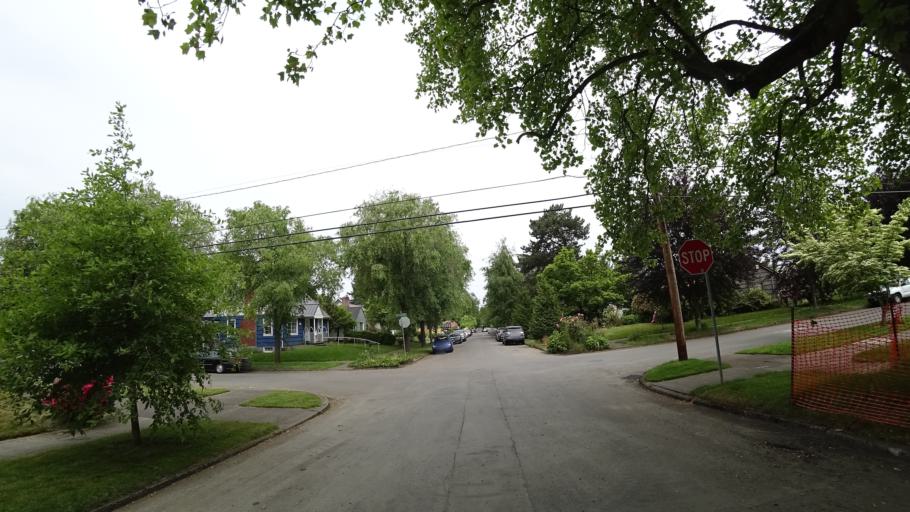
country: US
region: Oregon
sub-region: Multnomah County
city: Portland
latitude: 45.5682
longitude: -122.6403
